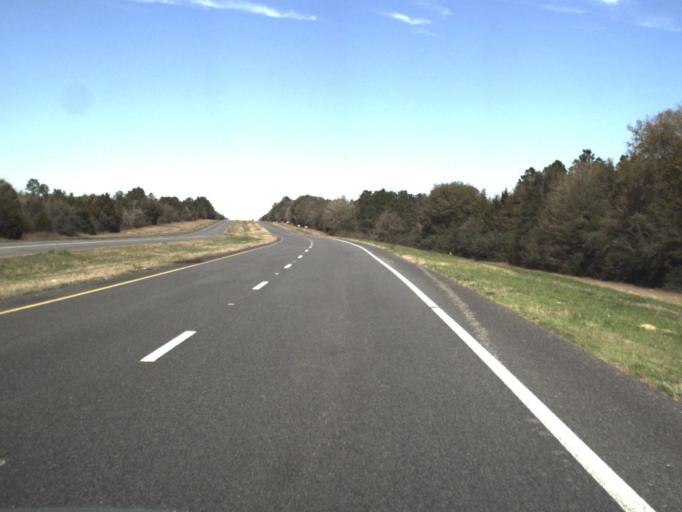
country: US
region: Florida
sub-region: Washington County
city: Chipley
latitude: 30.6122
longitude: -85.3960
